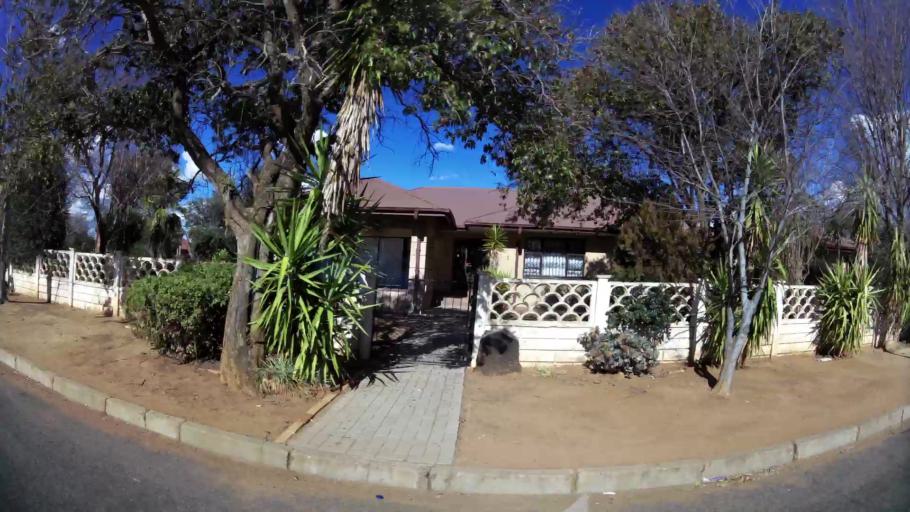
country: ZA
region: North-West
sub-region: Dr Kenneth Kaunda District Municipality
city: Klerksdorp
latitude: -26.8603
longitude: 26.6467
